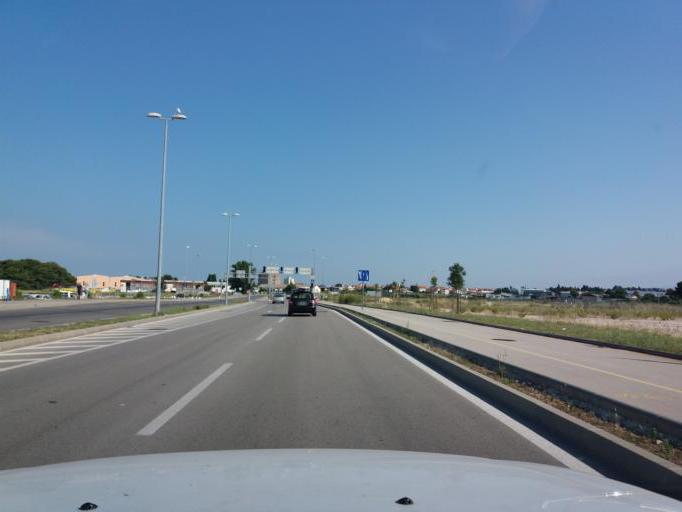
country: HR
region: Zadarska
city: Zadar
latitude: 44.0957
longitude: 15.2590
